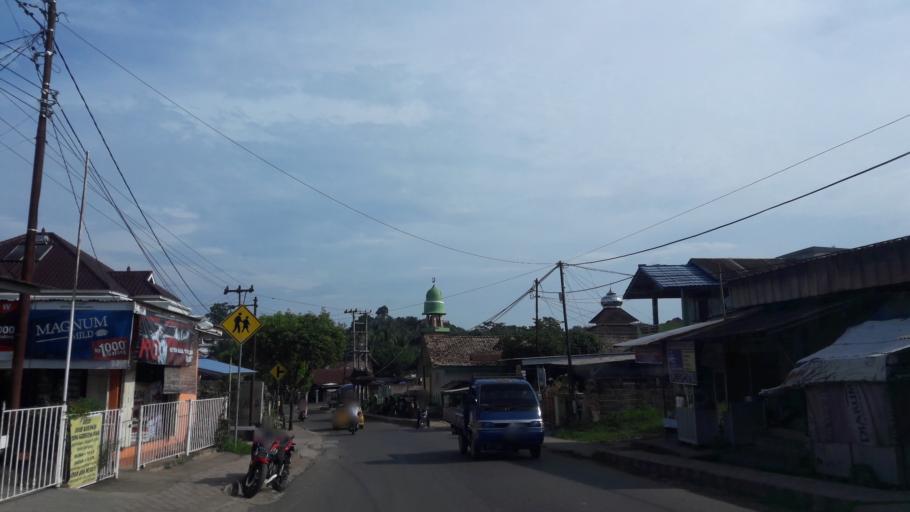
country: ID
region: South Sumatra
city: Gunungmegang Dalam
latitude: -3.2747
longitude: 103.8308
